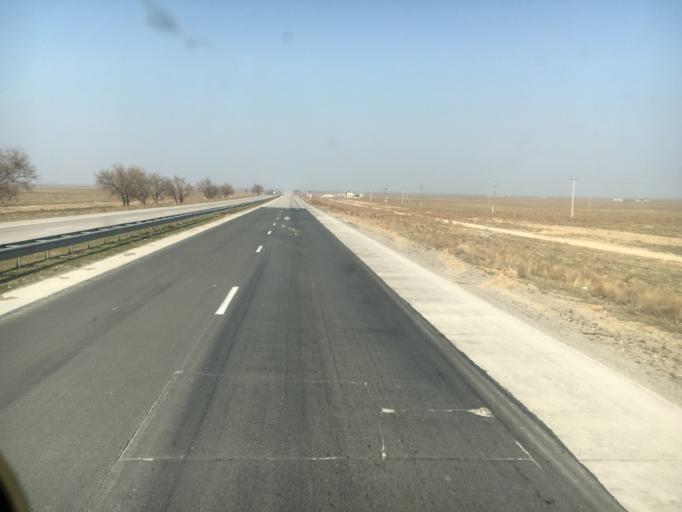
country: KZ
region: Ongtustik Qazaqstan
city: Temirlanovka
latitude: 42.8348
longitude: 69.1191
